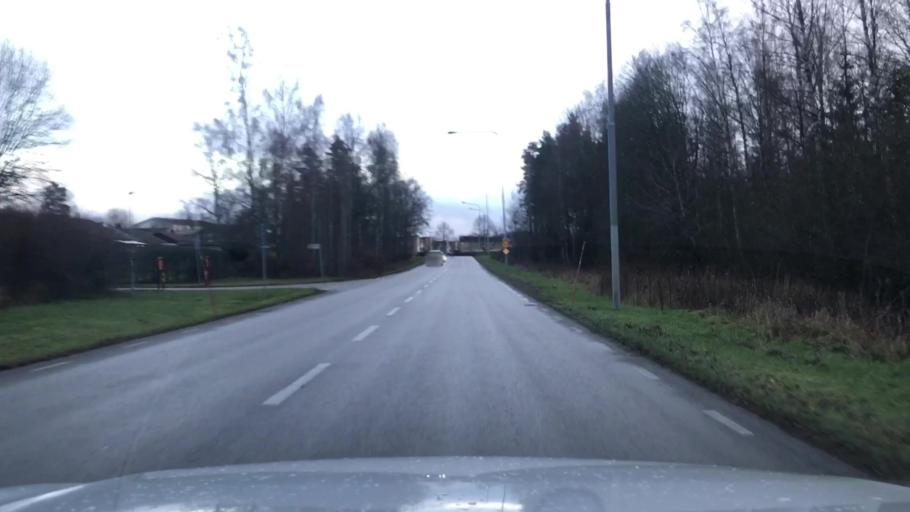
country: SE
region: OEstergoetland
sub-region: Linkopings Kommun
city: Malmslatt
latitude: 58.4136
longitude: 15.5551
